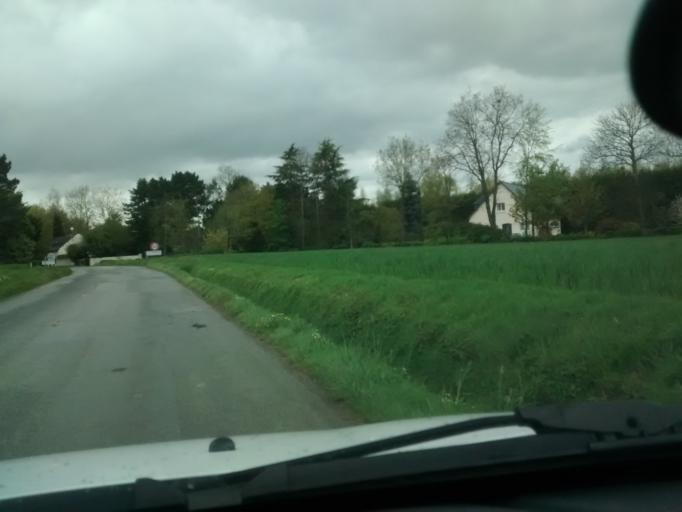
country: FR
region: Brittany
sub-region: Departement d'Ille-et-Vilaine
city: Noyal-sur-Vilaine
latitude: 48.0850
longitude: -1.5475
